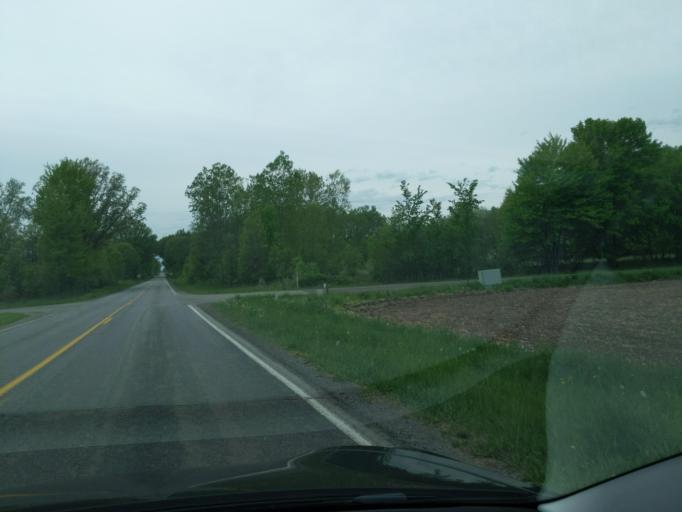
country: US
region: Michigan
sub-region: Ingham County
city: Leslie
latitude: 42.4475
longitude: -84.3736
